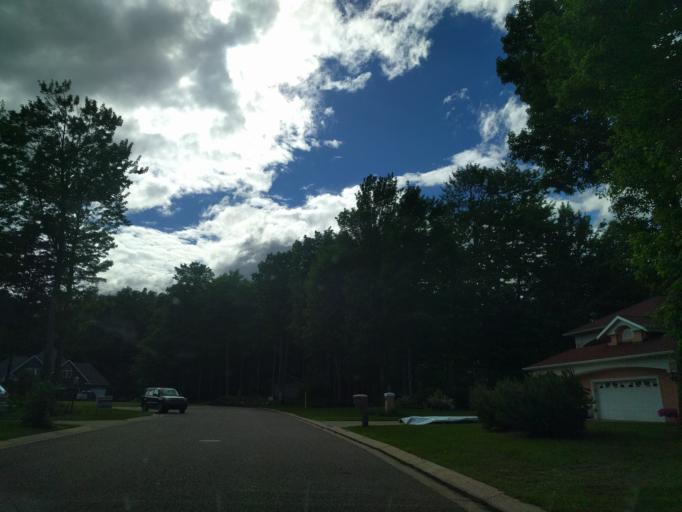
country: US
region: Michigan
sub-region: Marquette County
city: Marquette
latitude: 46.5307
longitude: -87.4199
